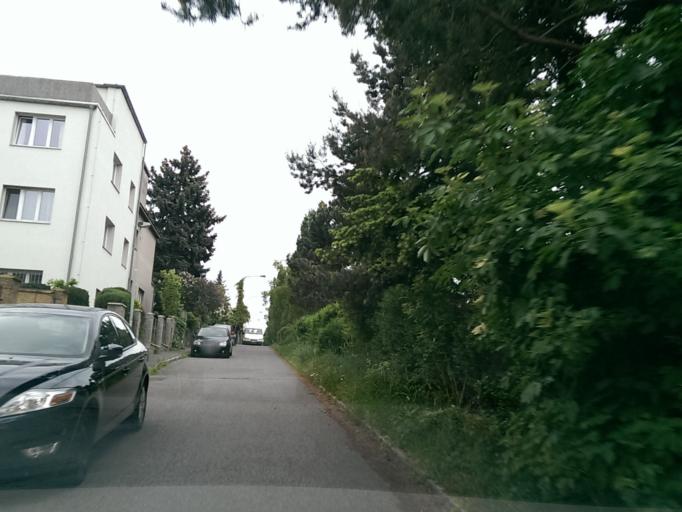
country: CZ
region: Praha
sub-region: Praha 8
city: Karlin
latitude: 50.0441
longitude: 14.4834
